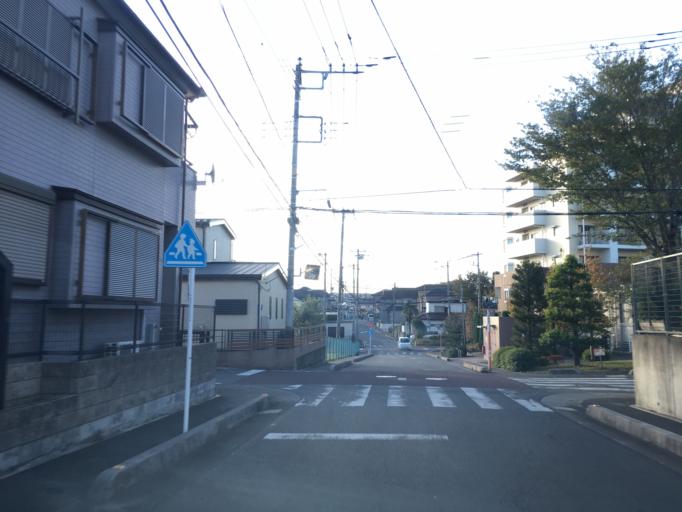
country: JP
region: Saitama
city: Tokorozawa
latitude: 35.7875
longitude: 139.4313
